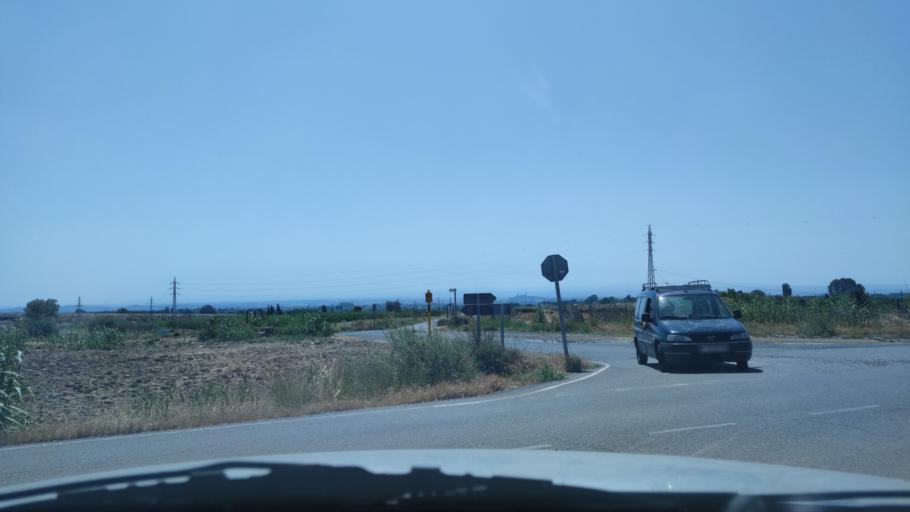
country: ES
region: Catalonia
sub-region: Provincia de Lleida
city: Alpicat
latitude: 41.6651
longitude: 0.5732
